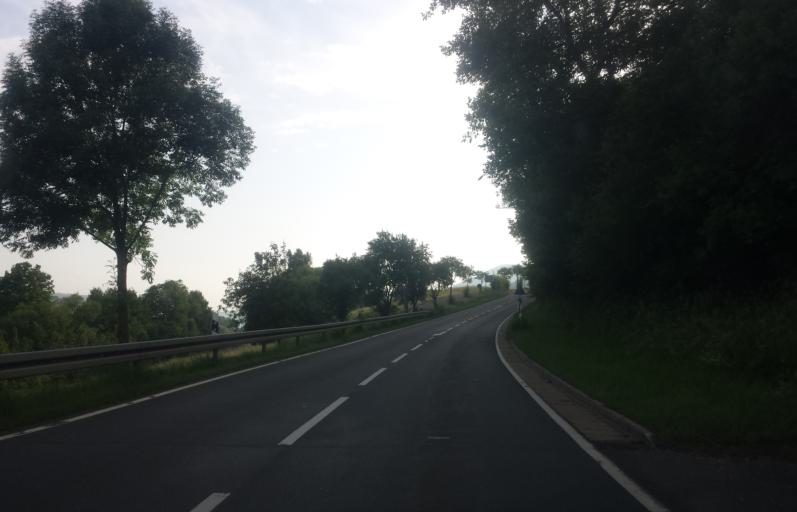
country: DE
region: Bavaria
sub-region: Upper Franconia
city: Ebermannstadt
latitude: 49.7840
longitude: 11.1960
